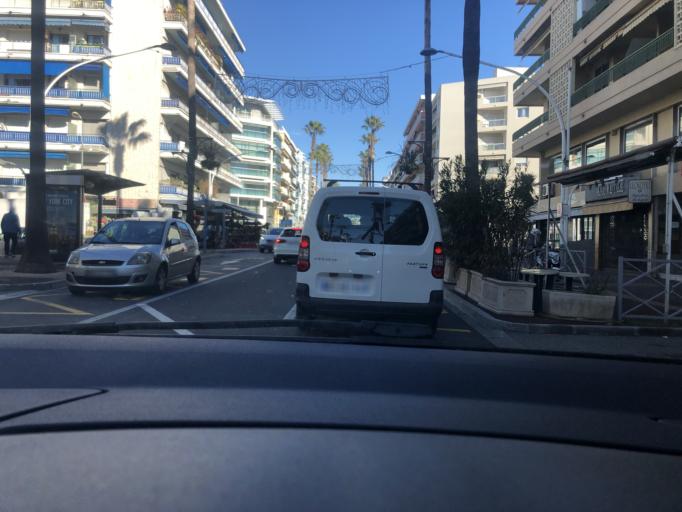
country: FR
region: Provence-Alpes-Cote d'Azur
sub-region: Departement des Alpes-Maritimes
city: Cagnes-sur-Mer
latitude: 43.6569
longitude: 7.1509
